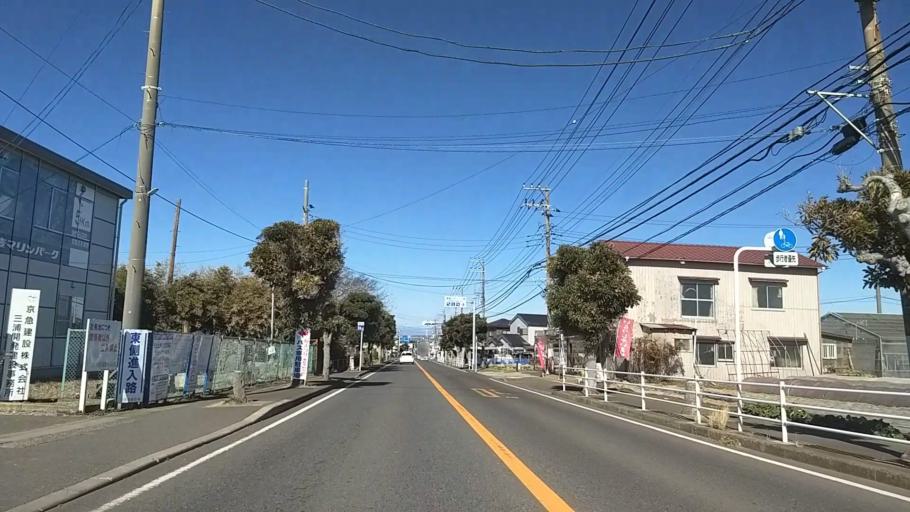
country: JP
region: Kanagawa
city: Miura
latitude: 35.1725
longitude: 139.6364
